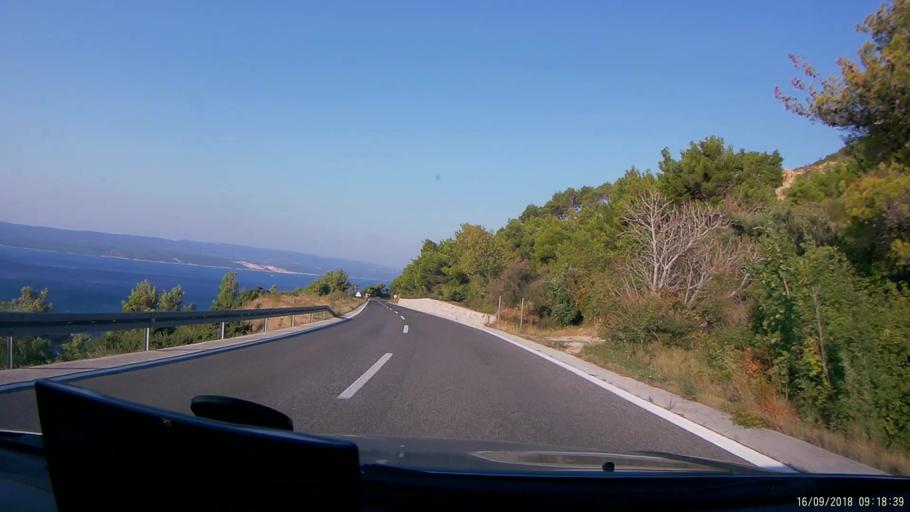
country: HR
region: Splitsko-Dalmatinska
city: Donja Brela
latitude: 43.4034
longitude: 16.8399
